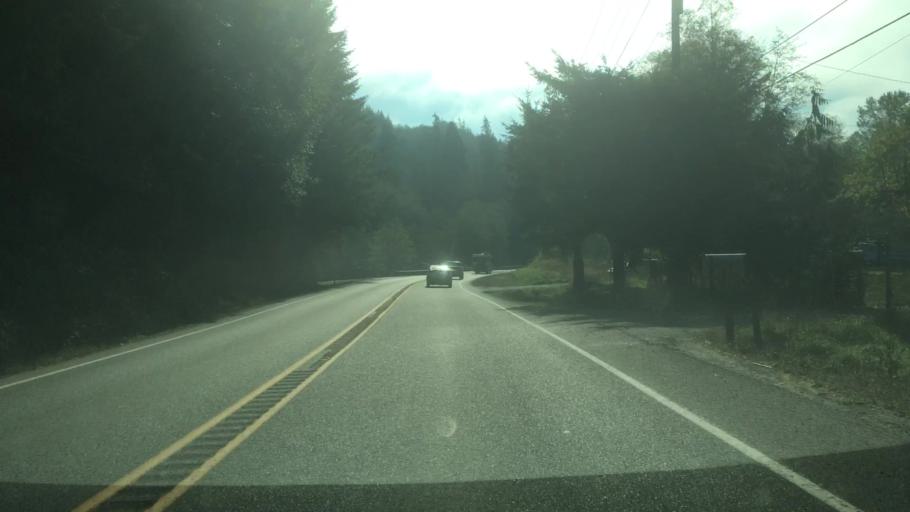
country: US
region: Washington
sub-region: Grays Harbor County
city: Montesano
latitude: 46.9522
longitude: -123.6119
